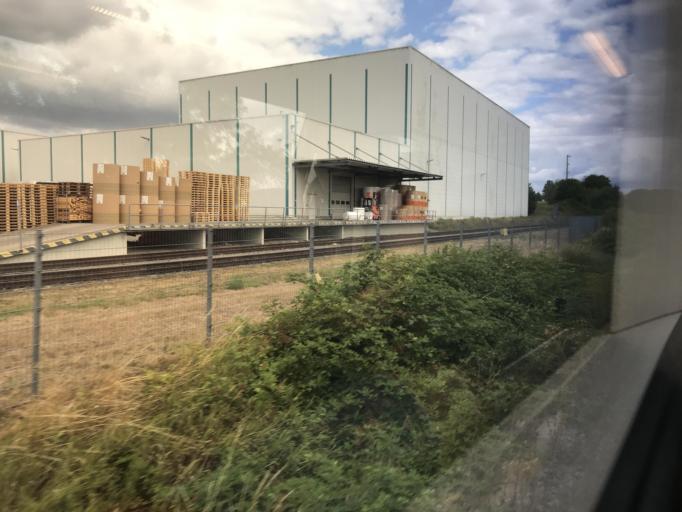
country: DE
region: Bavaria
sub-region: Regierungsbezirk Unterfranken
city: Fuchsstadt
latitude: 50.1258
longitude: 9.9379
